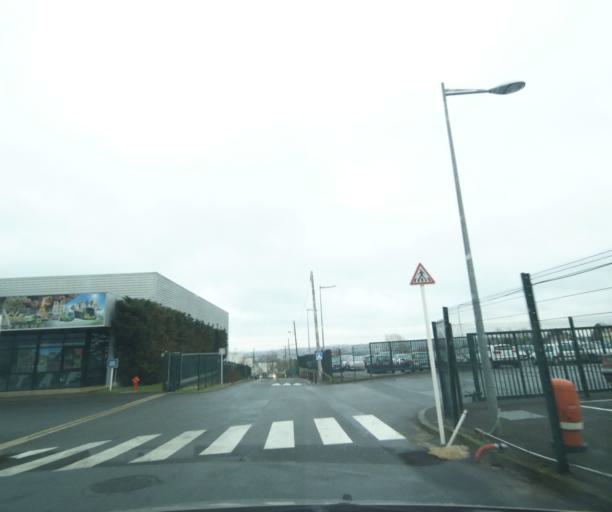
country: FR
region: Ile-de-France
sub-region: Departement du Val-de-Marne
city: Villeneuve-le-Roi
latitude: 48.7290
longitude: 2.4071
